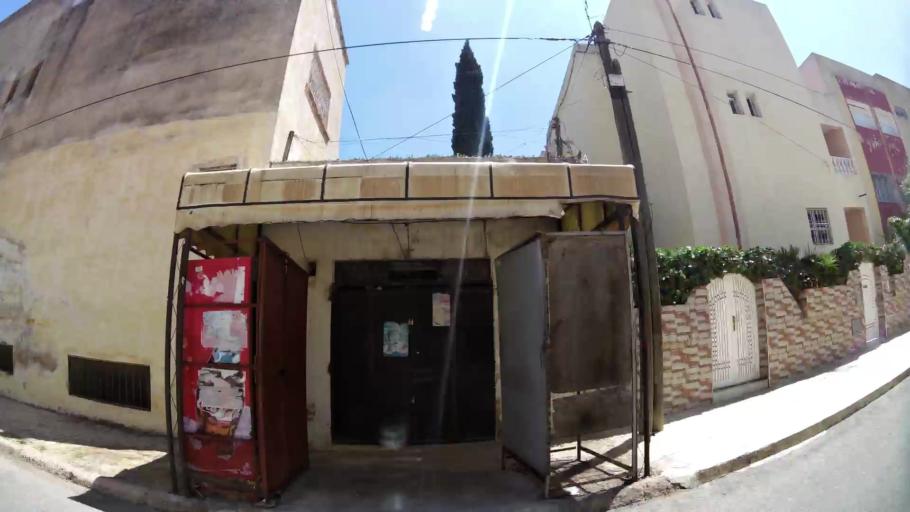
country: MA
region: Fes-Boulemane
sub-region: Fes
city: Fes
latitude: 34.0168
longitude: -5.0076
